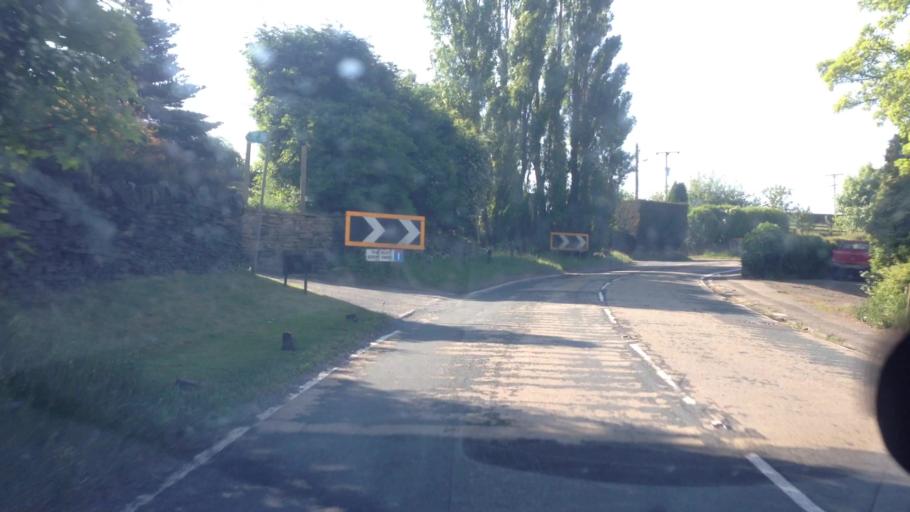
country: GB
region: England
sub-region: Kirklees
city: Mirfield
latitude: 53.6741
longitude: -1.7282
